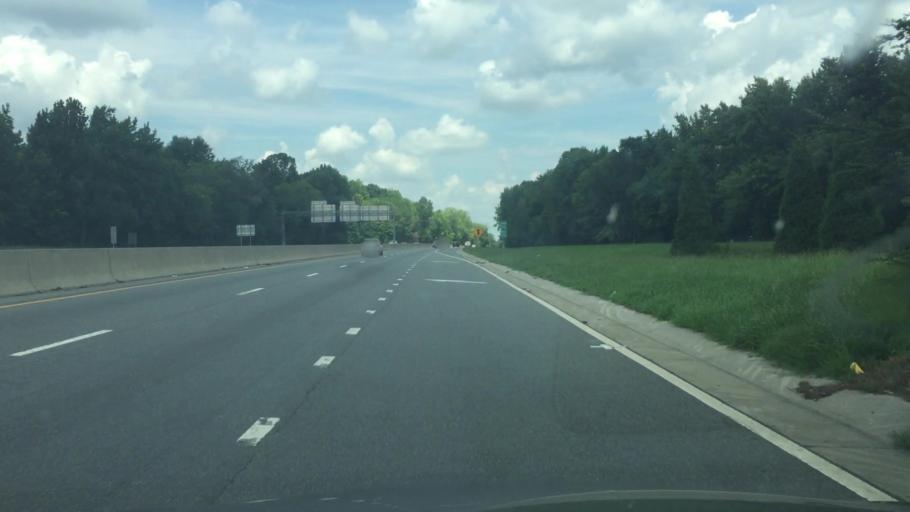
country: US
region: North Carolina
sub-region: Randolph County
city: Asheboro
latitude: 35.6879
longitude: -79.8308
